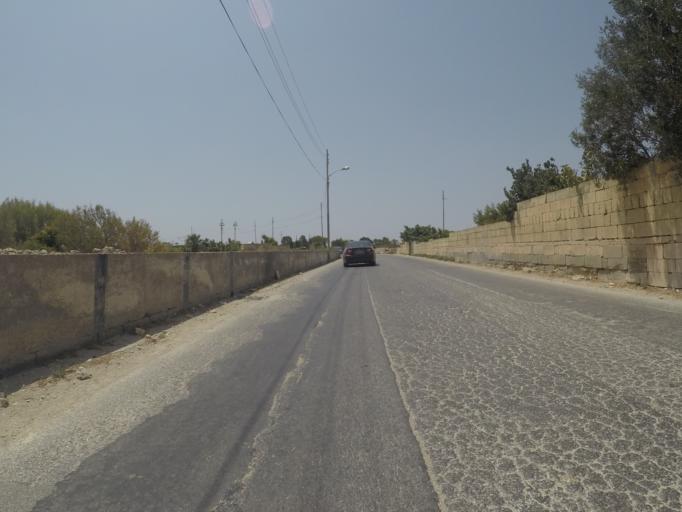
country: MT
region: Is-Siggiewi
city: Siggiewi
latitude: 35.8466
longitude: 14.4340
